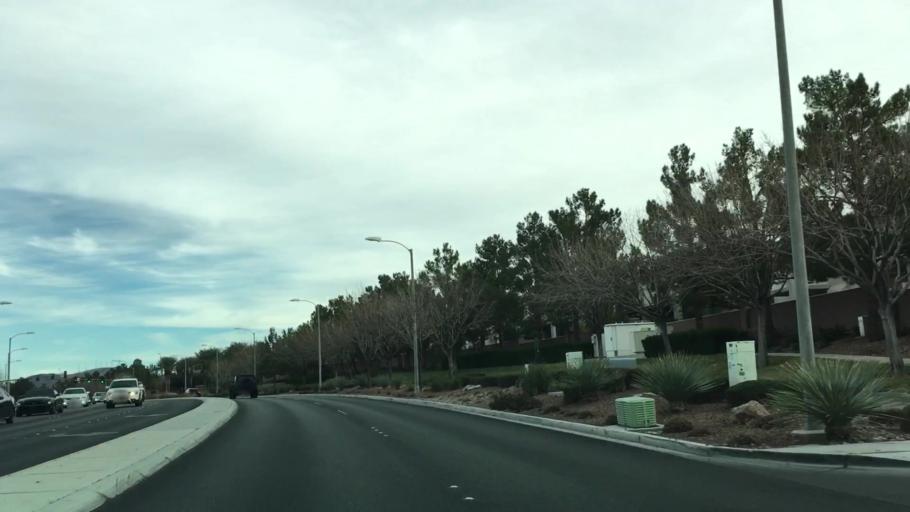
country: US
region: Nevada
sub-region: Clark County
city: Whitney
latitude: 36.0183
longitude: -115.0941
